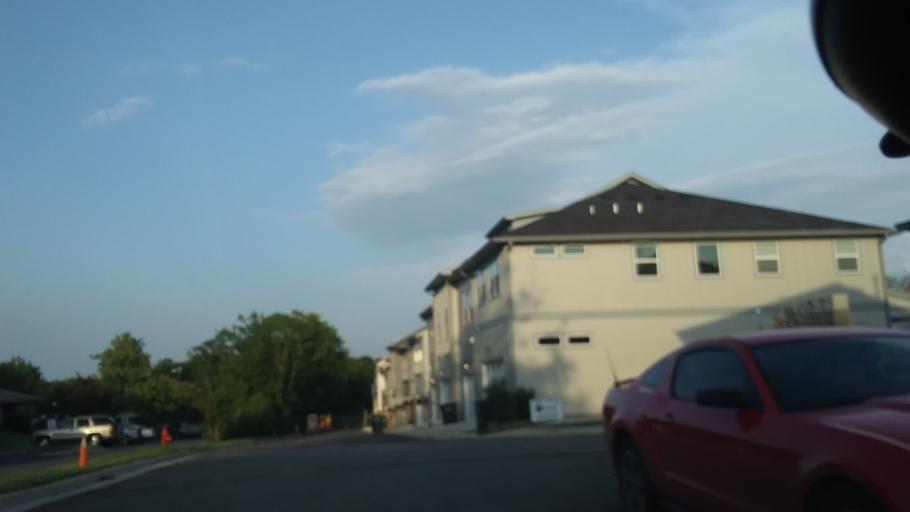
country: US
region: Tennessee
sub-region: Davidson County
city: Belle Meade
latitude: 36.1553
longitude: -86.8748
